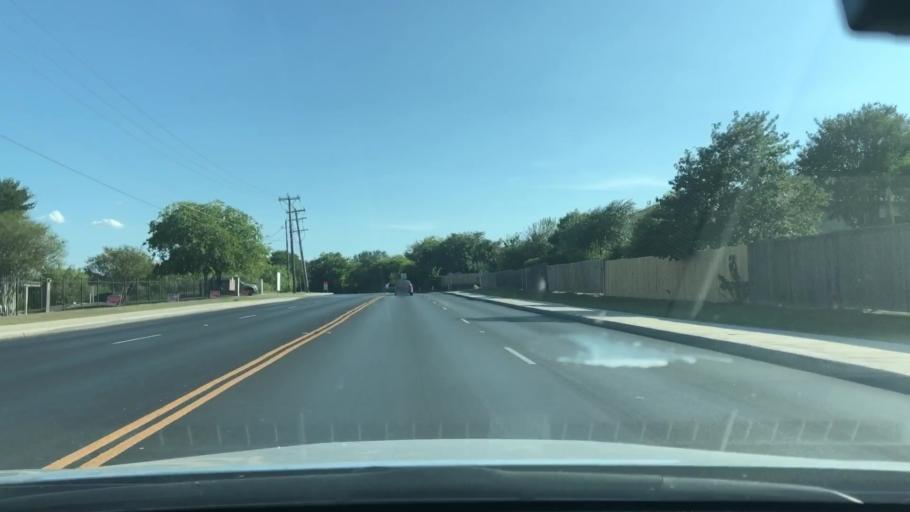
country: US
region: Texas
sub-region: Bexar County
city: Kirby
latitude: 29.4805
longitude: -98.3481
